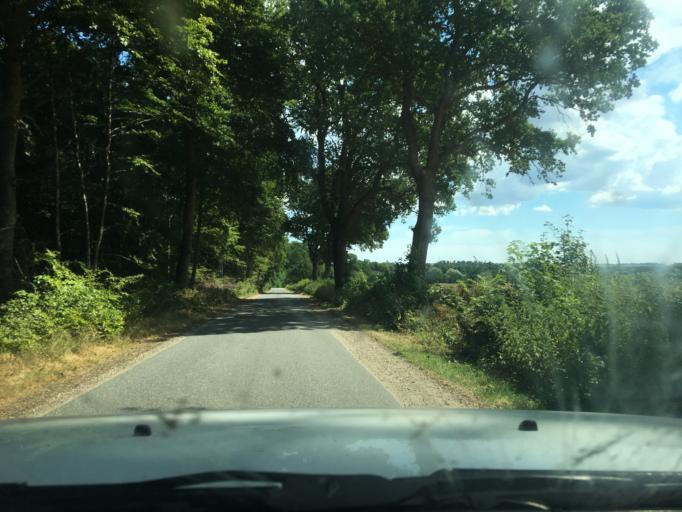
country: DK
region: Central Jutland
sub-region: Syddjurs Kommune
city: Hornslet
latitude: 56.3352
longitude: 10.3185
